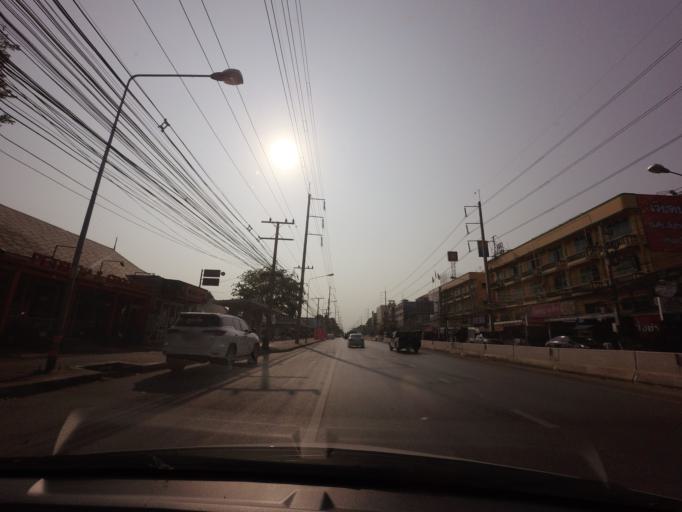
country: TH
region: Nakhon Pathom
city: Salaya
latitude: 13.8014
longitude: 100.3178
